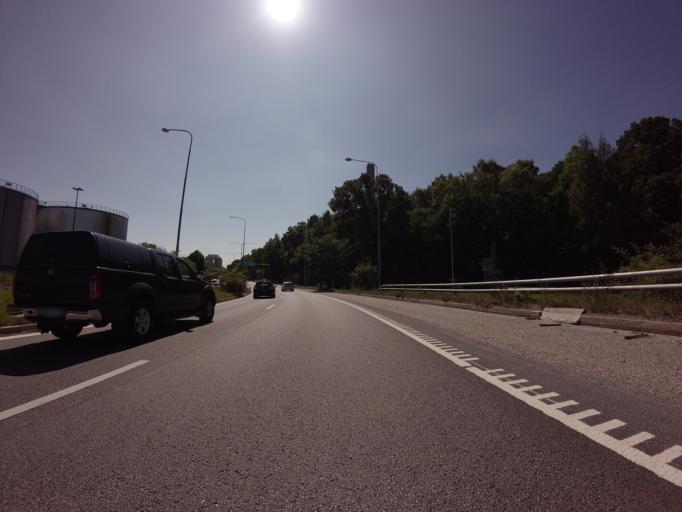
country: SE
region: Stockholm
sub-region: Stockholms Kommun
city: OEstermalm
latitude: 59.3567
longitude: 18.1040
